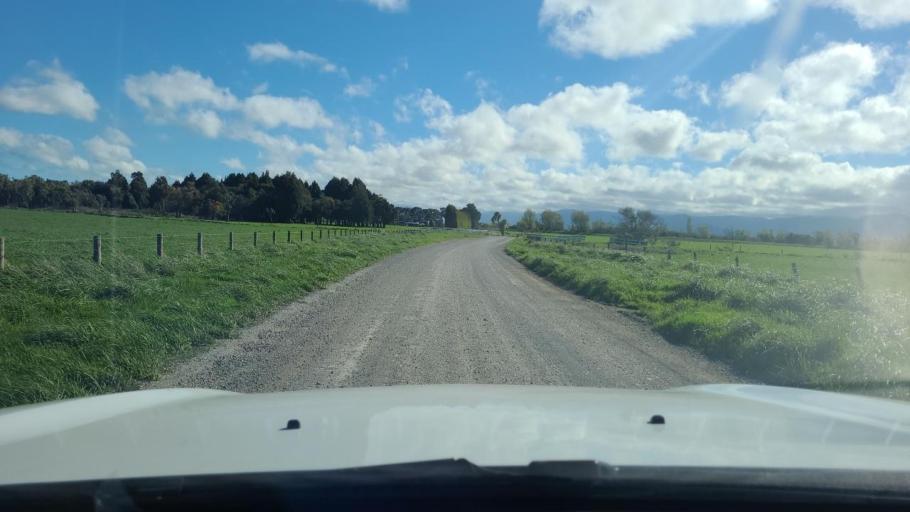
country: NZ
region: Wellington
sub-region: South Wairarapa District
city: Waipawa
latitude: -41.1606
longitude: 175.3631
